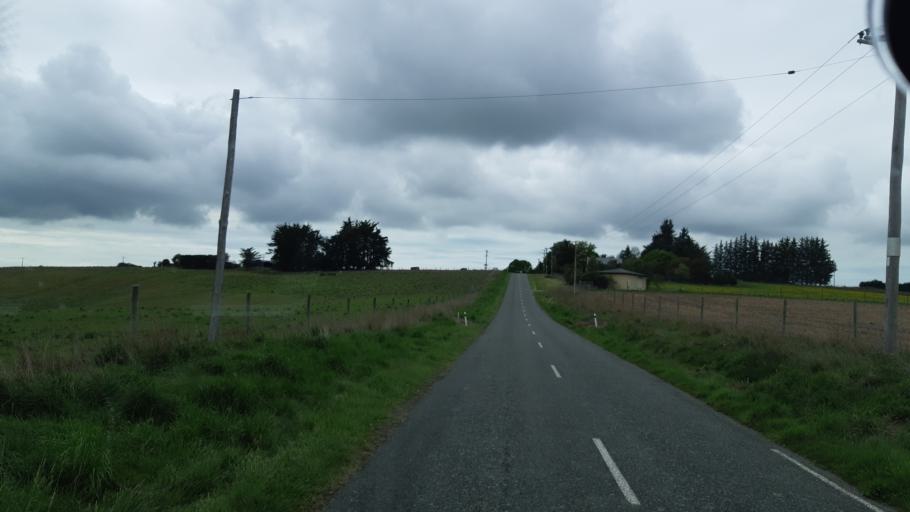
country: NZ
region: Canterbury
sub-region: Timaru District
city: Pleasant Point
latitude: -44.3302
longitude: 171.1545
